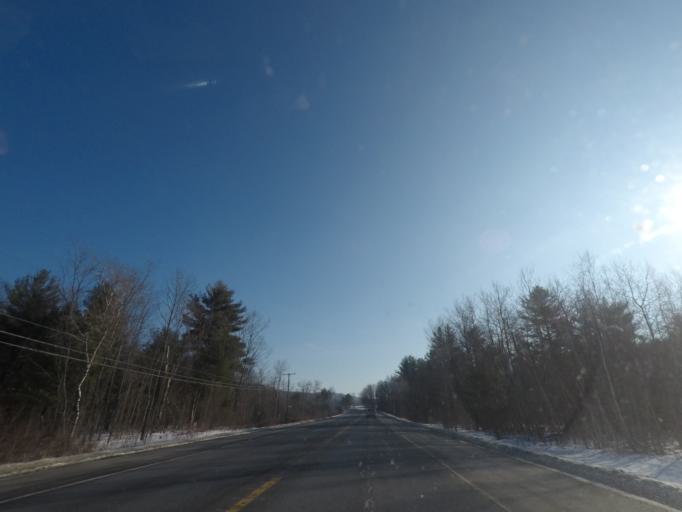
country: US
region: Massachusetts
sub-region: Berkshire County
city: Lanesborough
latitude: 42.5352
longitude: -73.3588
